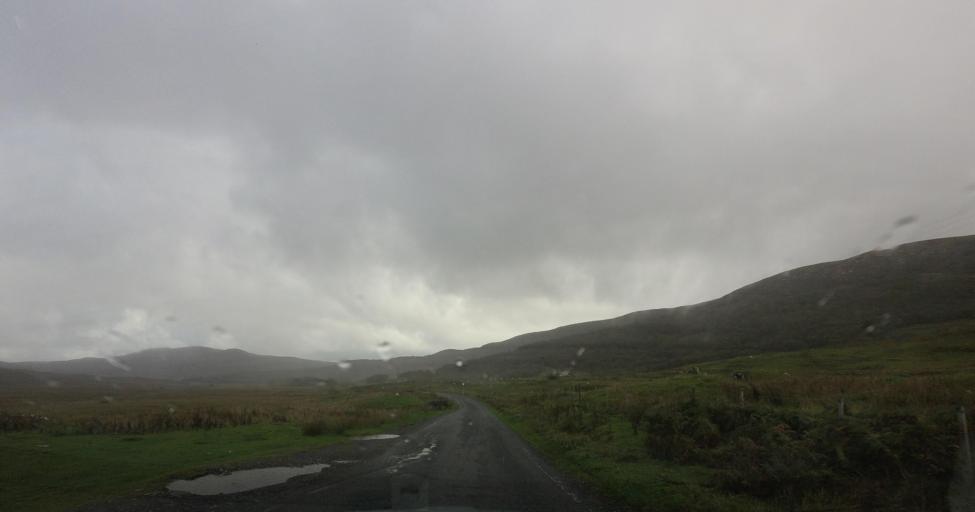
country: GB
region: Scotland
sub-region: Highland
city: Portree
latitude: 57.2079
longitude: -5.9845
